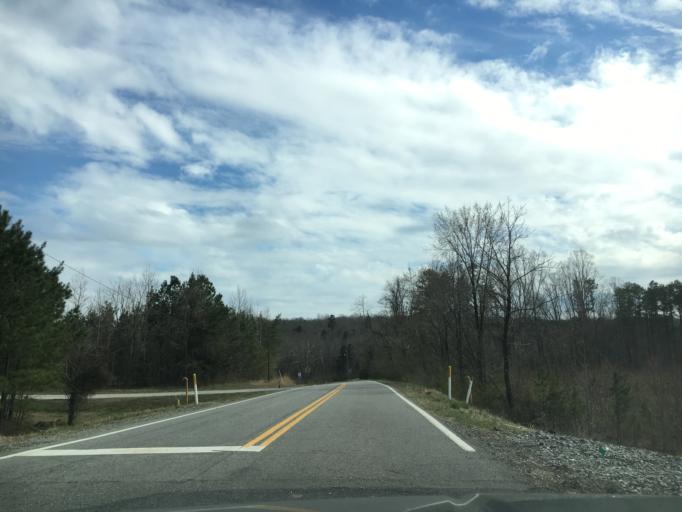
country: US
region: Virginia
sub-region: Halifax County
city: Halifax
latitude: 36.7657
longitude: -78.9163
